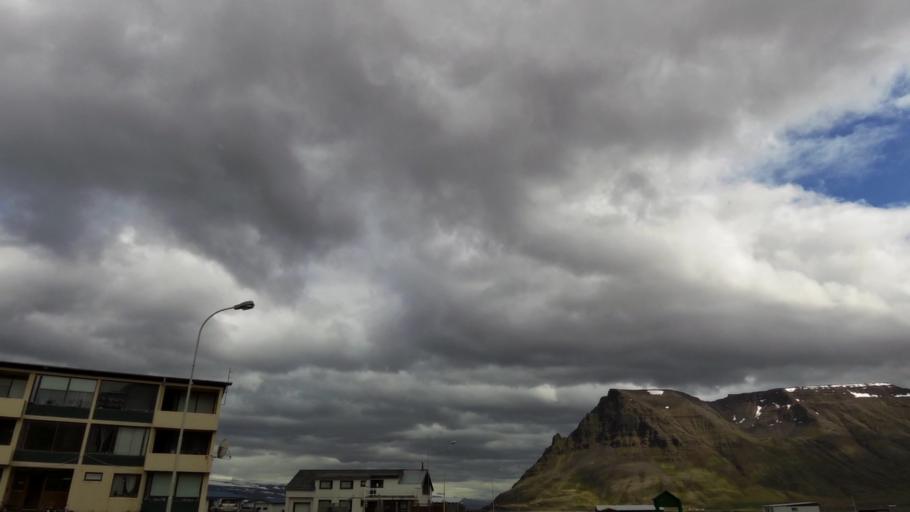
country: IS
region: Westfjords
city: Isafjoerdur
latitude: 66.1587
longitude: -23.2618
